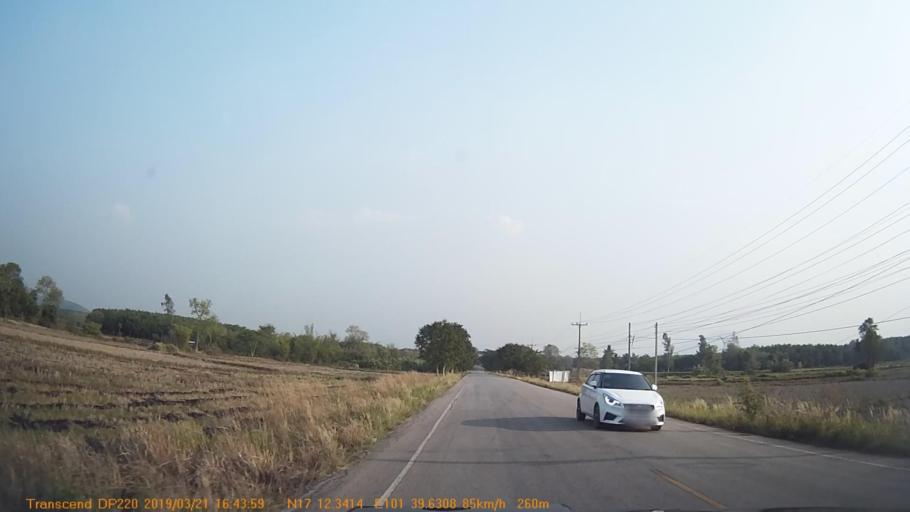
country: TH
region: Loei
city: Phu Luang
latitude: 17.2054
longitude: 101.6606
